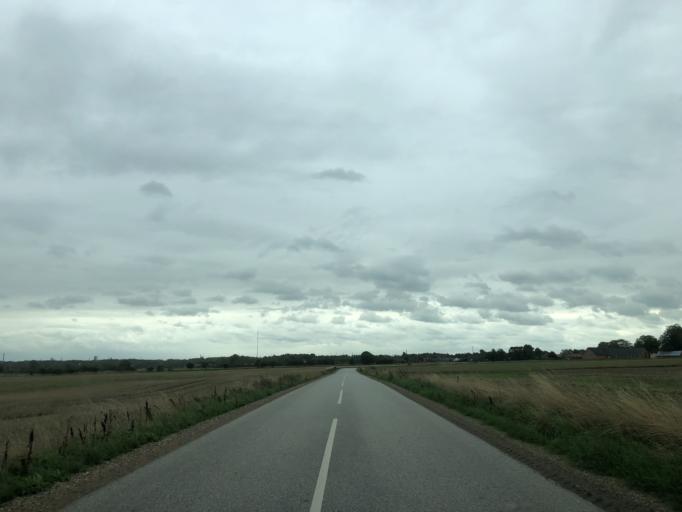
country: DK
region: Central Jutland
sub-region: Herning Kommune
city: Snejbjerg
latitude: 56.1426
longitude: 8.9031
